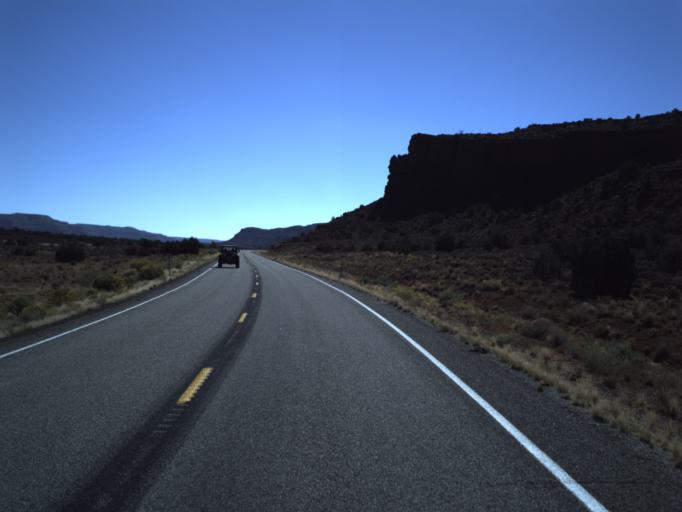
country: US
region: Utah
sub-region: San Juan County
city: Blanding
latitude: 37.6930
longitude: -110.2290
